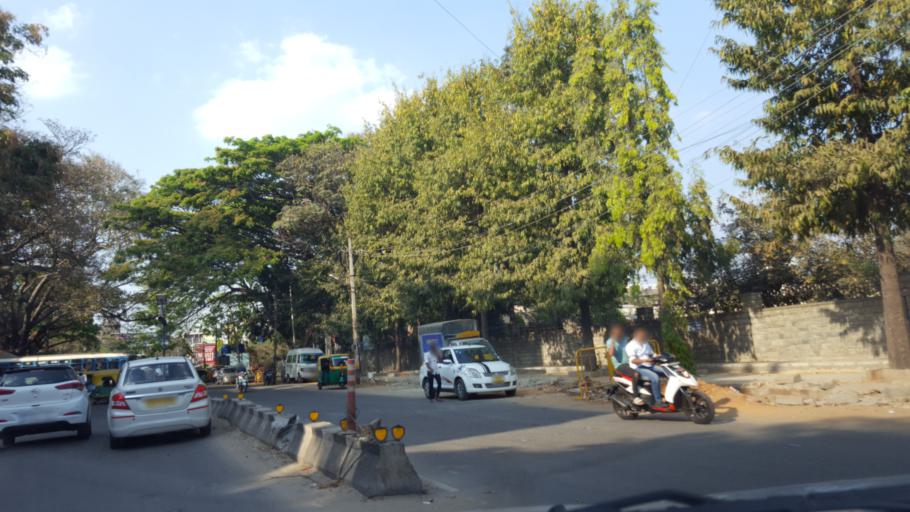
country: IN
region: Karnataka
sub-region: Bangalore Urban
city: Bangalore
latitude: 12.9263
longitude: 77.5971
